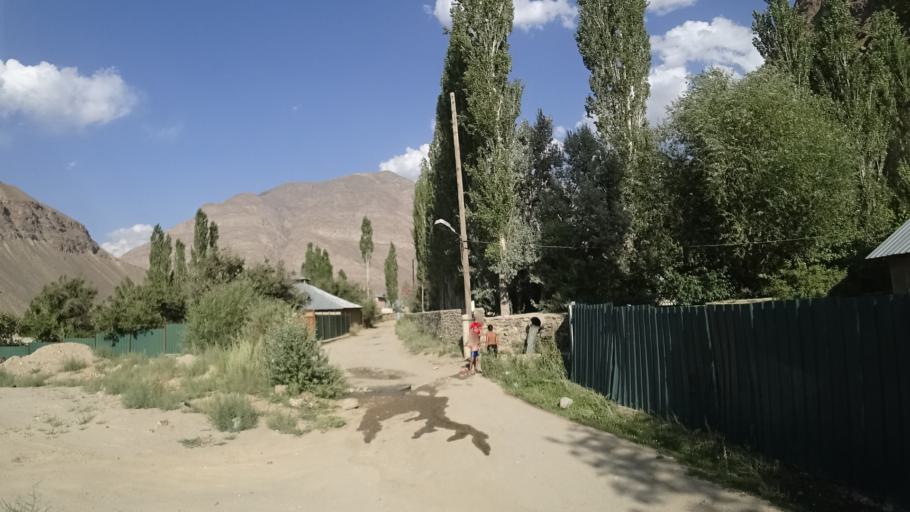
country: TJ
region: Gorno-Badakhshan
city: Khorugh
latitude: 37.4871
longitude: 71.5610
